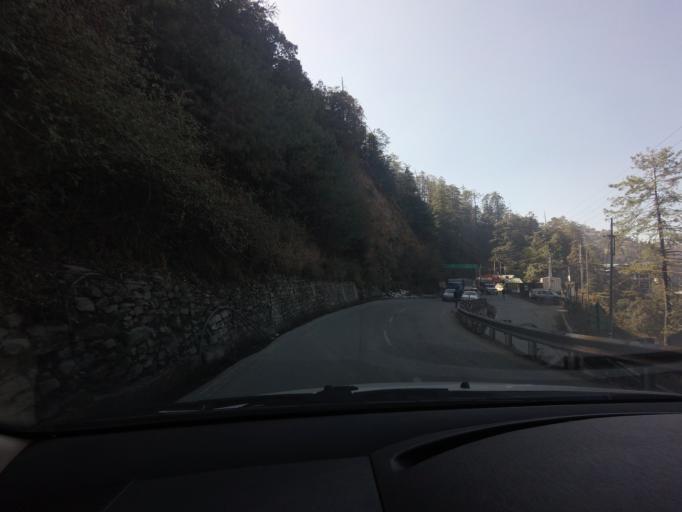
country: IN
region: Himachal Pradesh
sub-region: Shimla
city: Shimla
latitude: 31.1101
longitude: 77.2168
